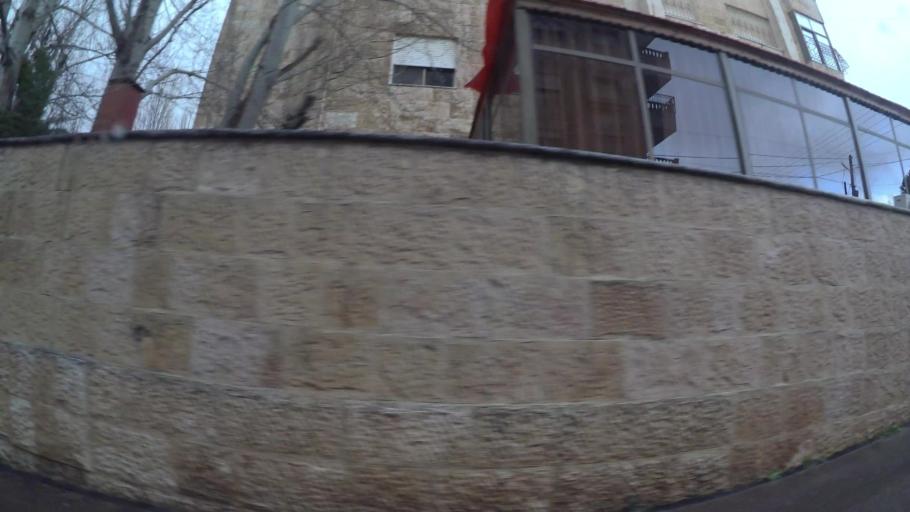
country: JO
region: Amman
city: Al Jubayhah
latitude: 32.0326
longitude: 35.8609
